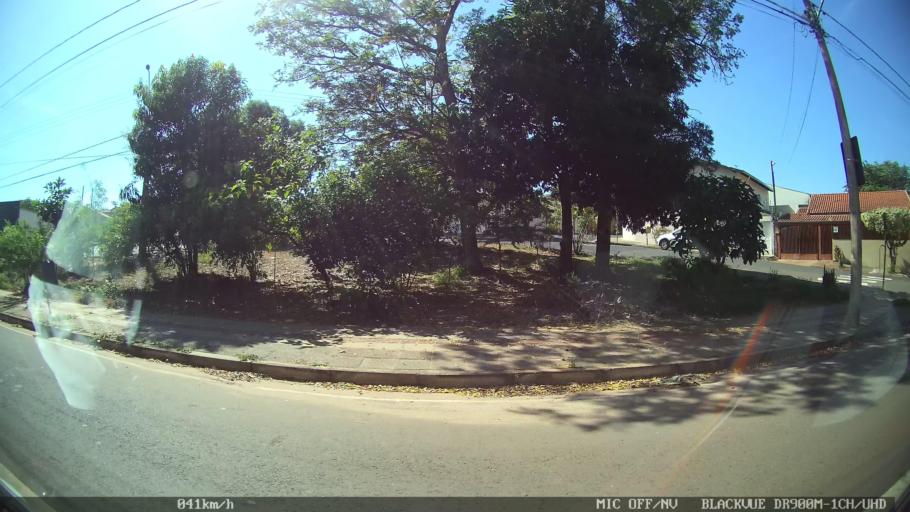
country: BR
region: Sao Paulo
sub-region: Sao Jose Do Rio Preto
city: Sao Jose do Rio Preto
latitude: -20.7767
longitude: -49.3953
